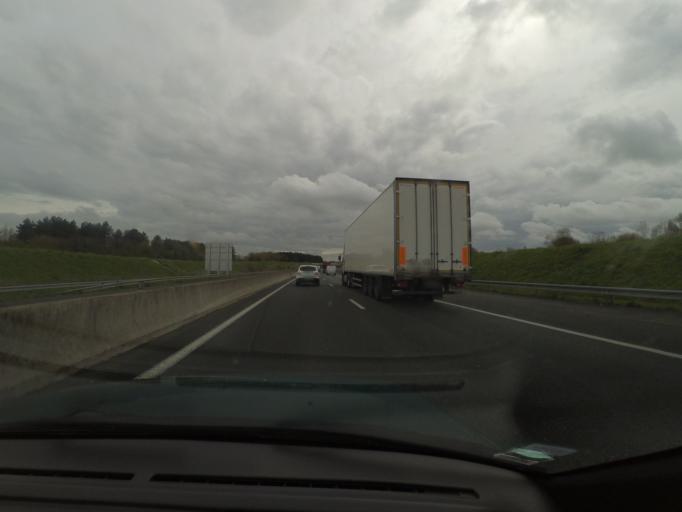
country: FR
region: Pays de la Loire
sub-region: Departement de Maine-et-Loire
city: Avrille
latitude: 47.4948
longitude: -0.6078
